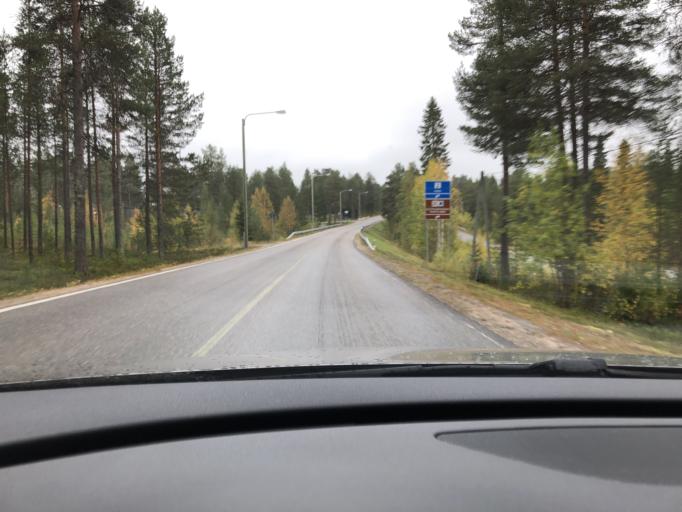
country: FI
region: Lapland
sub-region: Itae-Lappi
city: Posio
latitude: 66.1154
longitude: 28.1824
